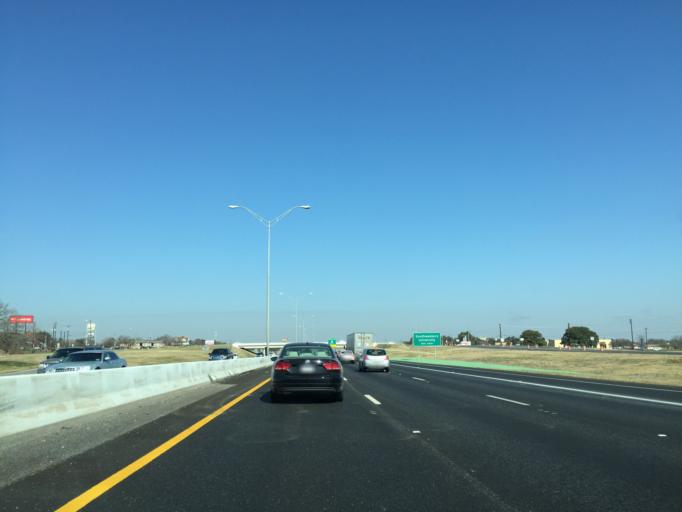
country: US
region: Texas
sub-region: Williamson County
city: Georgetown
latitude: 30.6182
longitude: -97.6888
